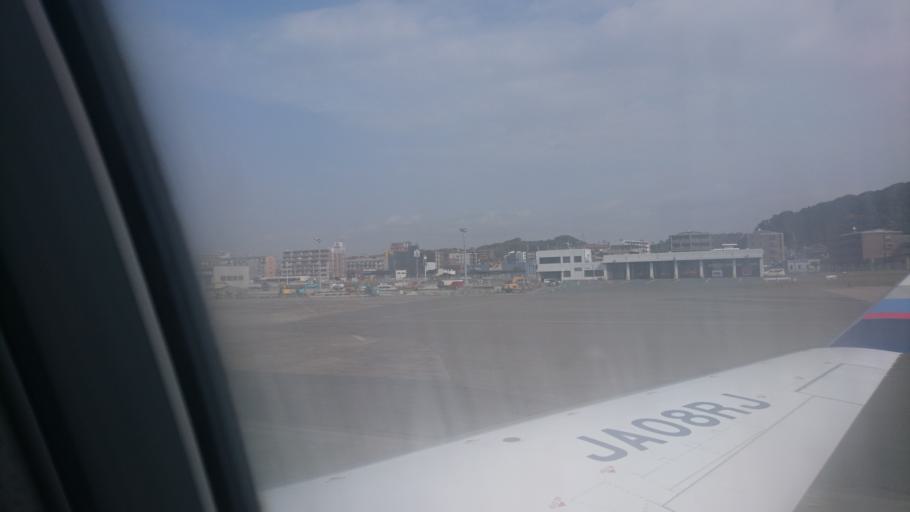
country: JP
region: Fukuoka
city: Fukuoka-shi
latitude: 33.5851
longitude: 130.4536
